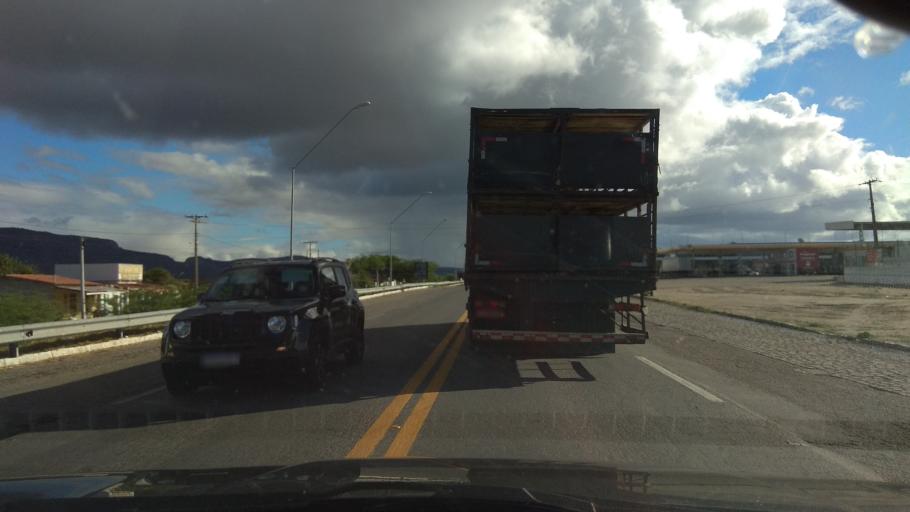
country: BR
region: Bahia
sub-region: Castro Alves
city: Castro Alves
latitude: -12.6970
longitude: -39.7055
